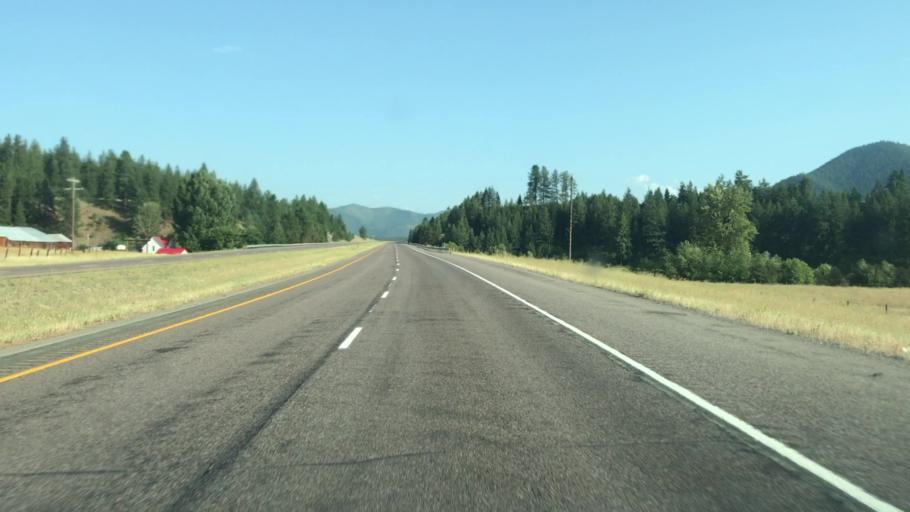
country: US
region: Montana
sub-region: Mineral County
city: Superior
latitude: 47.0548
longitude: -114.7603
